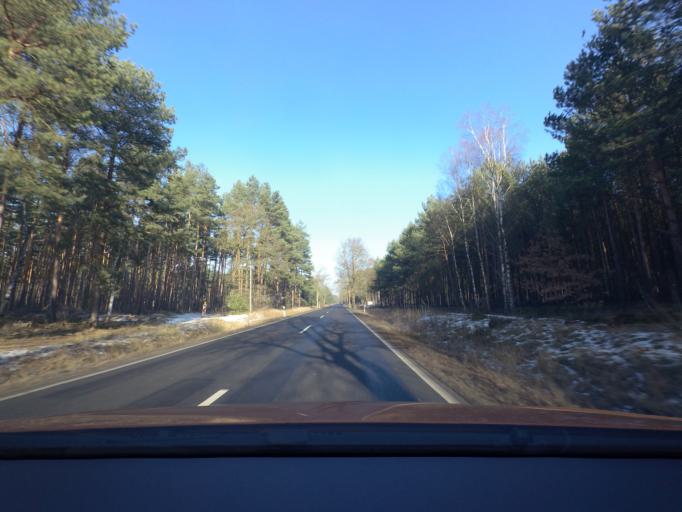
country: DE
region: Brandenburg
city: Glienicke
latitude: 52.7040
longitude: 13.3661
